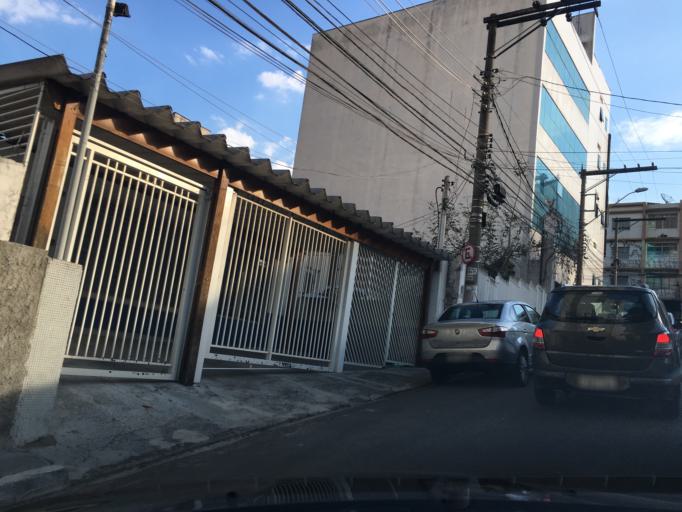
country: BR
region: Sao Paulo
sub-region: Guarulhos
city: Guarulhos
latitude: -23.4663
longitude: -46.5278
